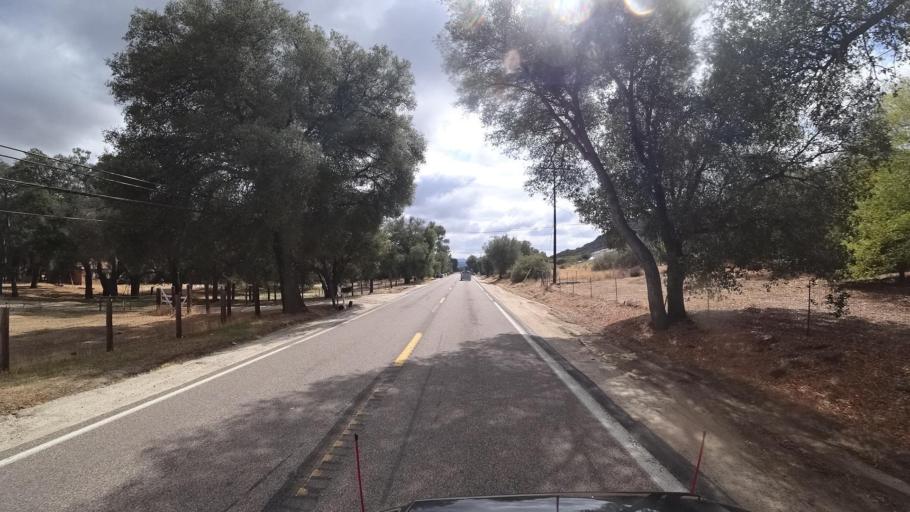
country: US
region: California
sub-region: San Diego County
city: Campo
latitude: 32.6618
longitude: -116.4880
